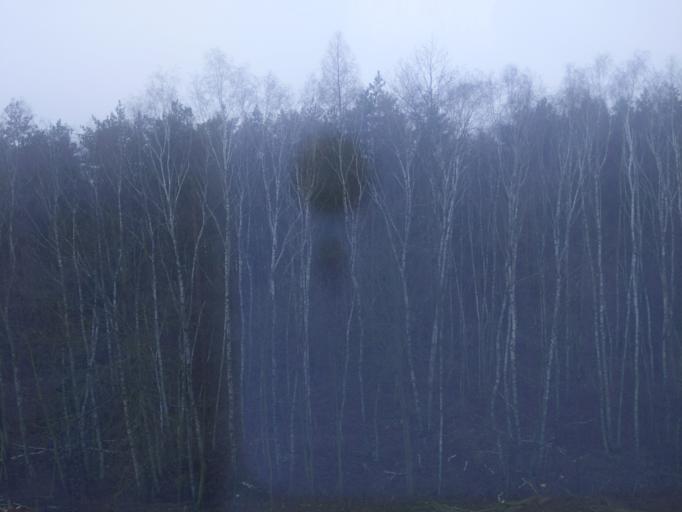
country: DE
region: Saxony
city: Albertstadt
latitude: 51.1237
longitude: 13.7979
